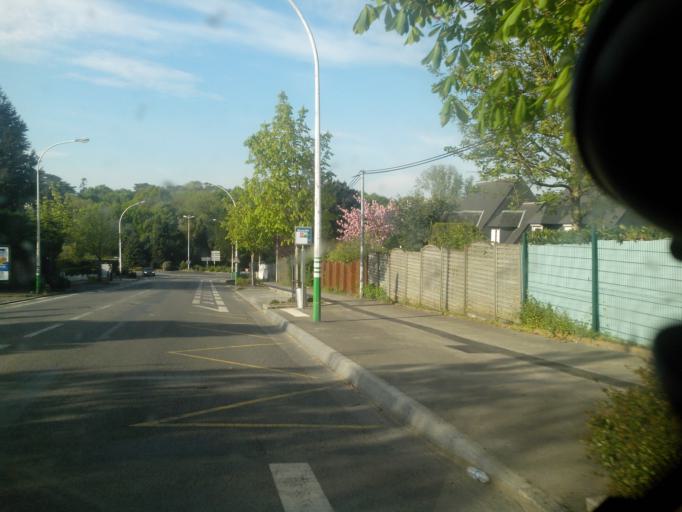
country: FR
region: Pays de la Loire
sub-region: Departement de la Loire-Atlantique
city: Orvault
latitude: 47.2382
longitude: -1.6113
